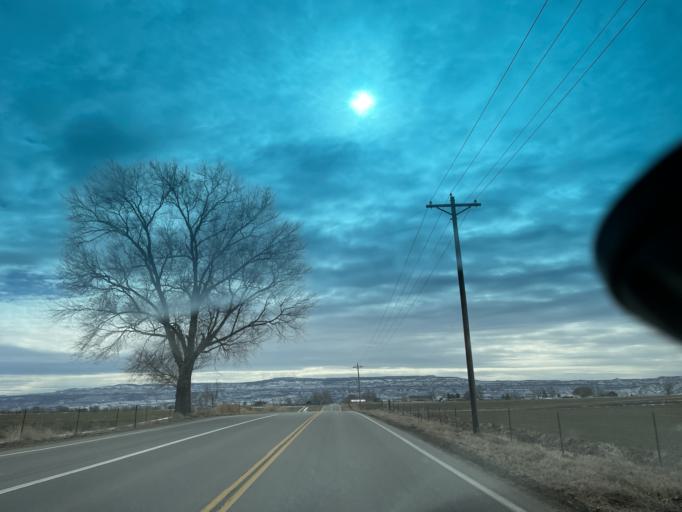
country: US
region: Colorado
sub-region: Mesa County
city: Loma
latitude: 39.2168
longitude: -108.8130
